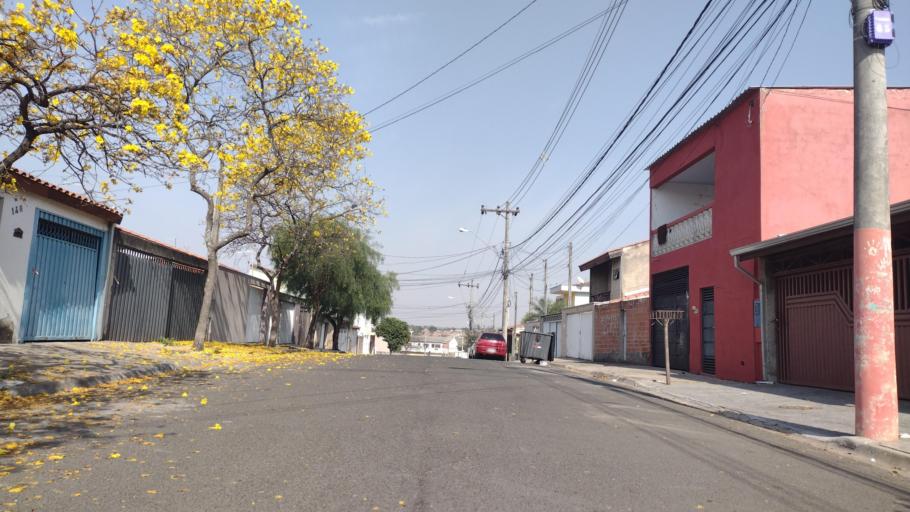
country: BR
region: Sao Paulo
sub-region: Sorocaba
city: Sorocaba
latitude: -23.4279
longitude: -47.4656
